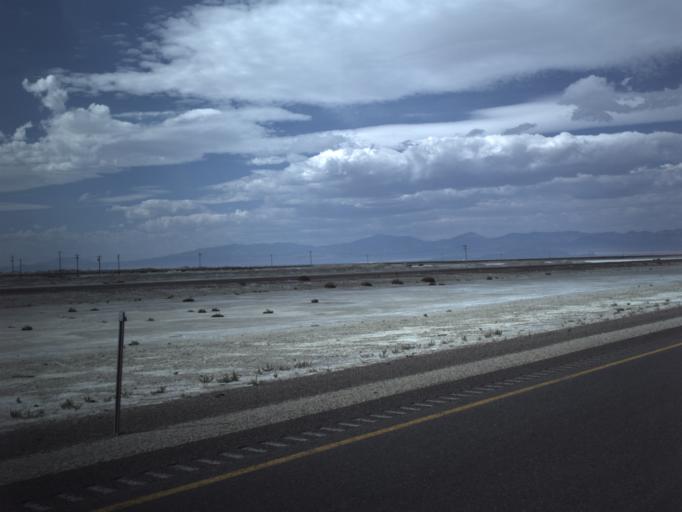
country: US
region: Utah
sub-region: Tooele County
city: Wendover
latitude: 40.7387
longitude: -113.8173
